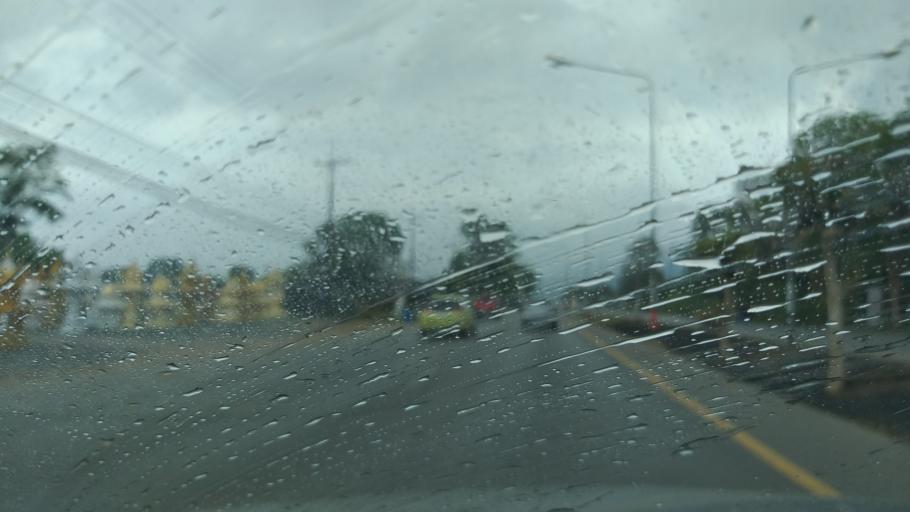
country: TH
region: Chanthaburi
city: Khlung
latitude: 12.4559
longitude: 102.2369
